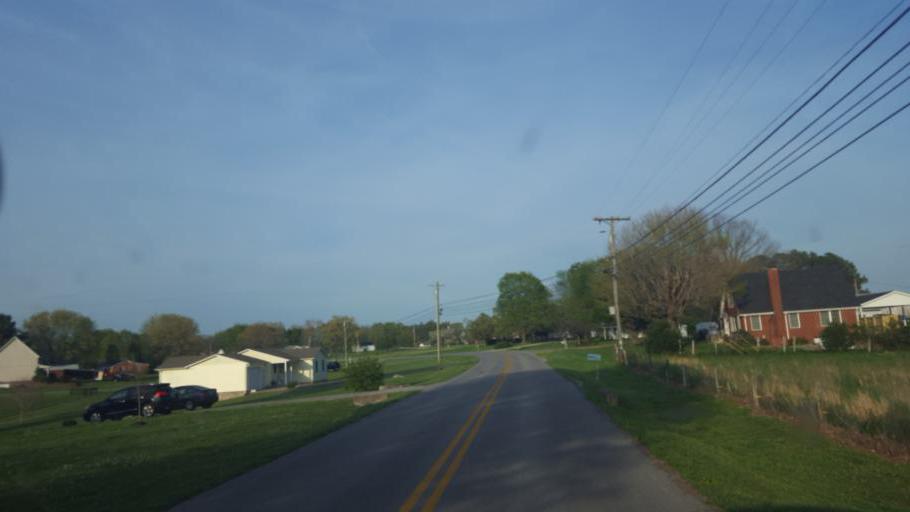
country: US
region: Kentucky
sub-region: Barren County
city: Glasgow
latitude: 36.9452
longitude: -85.9770
